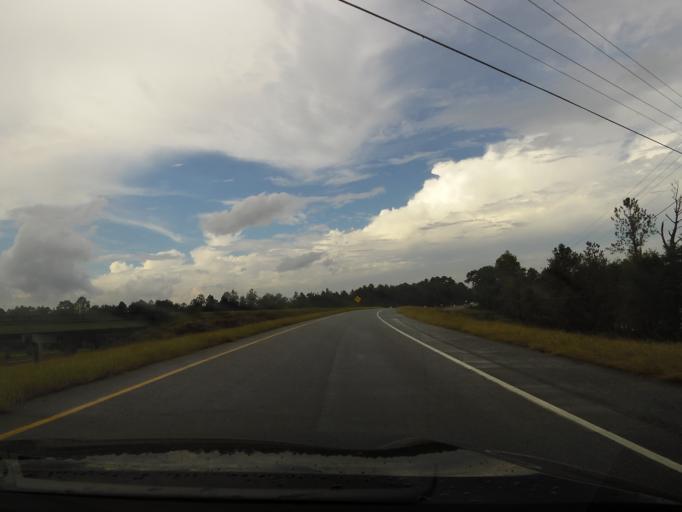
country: US
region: Georgia
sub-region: Wayne County
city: Jesup
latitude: 31.6227
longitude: -81.8668
